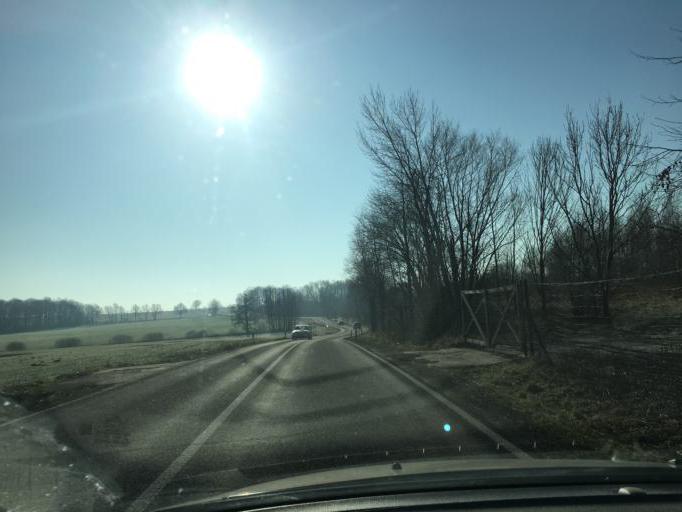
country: DE
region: Saxony
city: Otterwisch
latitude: 51.1926
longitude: 12.6095
